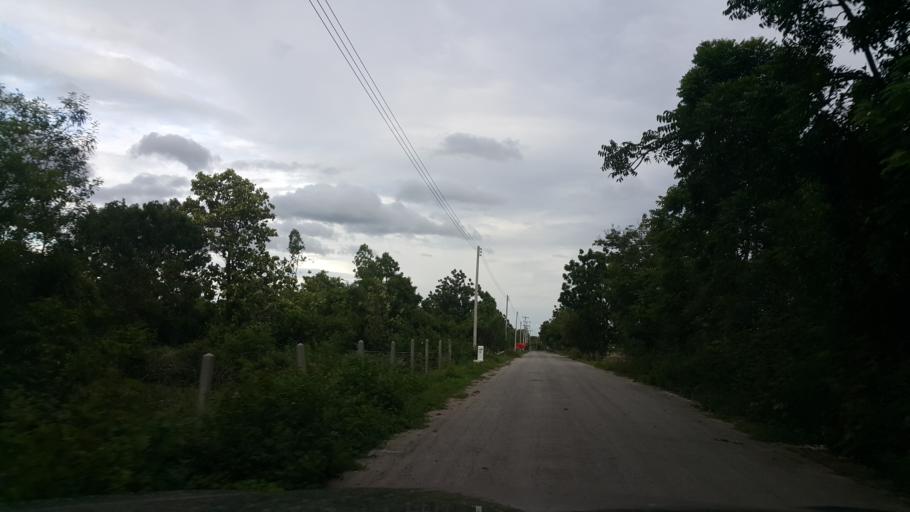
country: TH
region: Sukhothai
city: Thung Saliam
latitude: 17.1745
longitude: 99.4829
